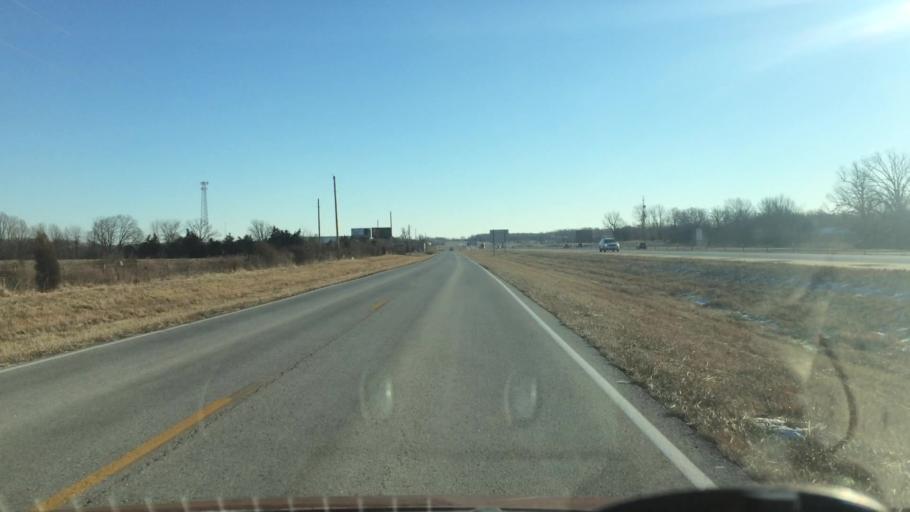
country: US
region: Missouri
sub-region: Greene County
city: Strafford
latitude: 37.2709
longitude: -93.0939
